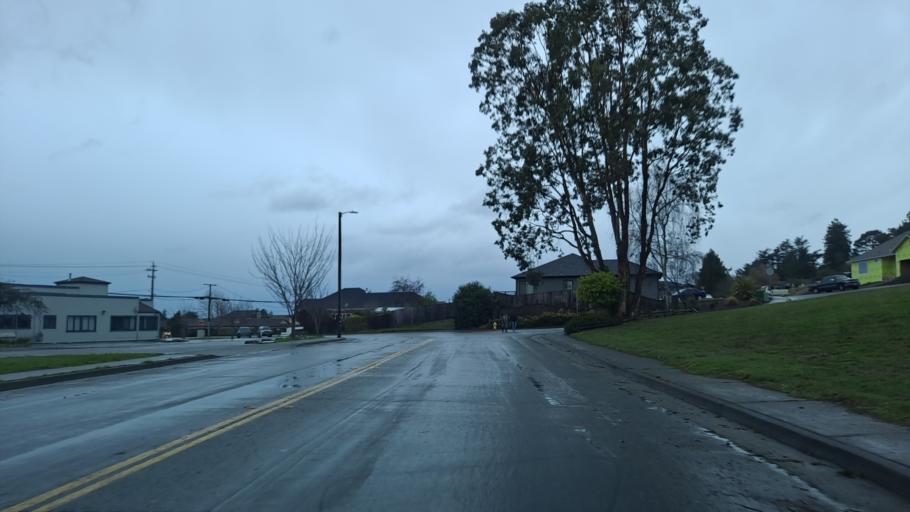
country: US
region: California
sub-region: Humboldt County
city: Fortuna
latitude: 40.5930
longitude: -124.1384
